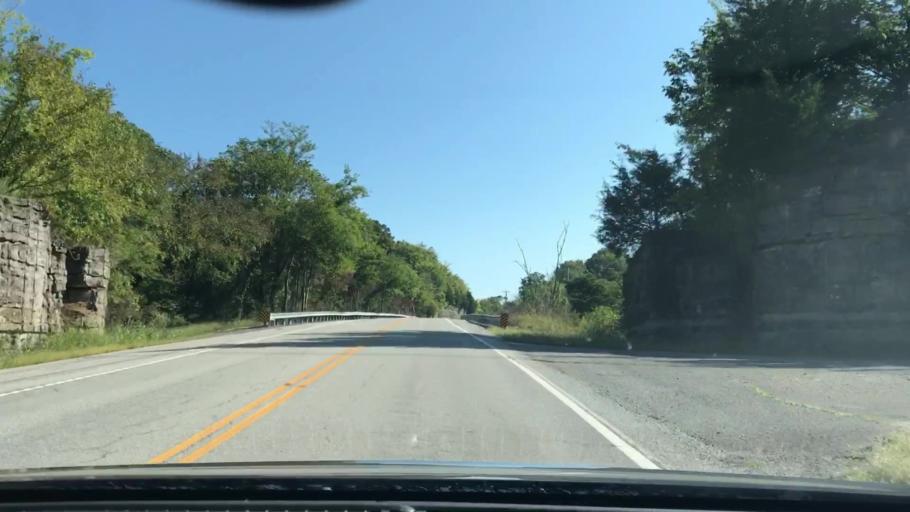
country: US
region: Tennessee
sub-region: Jackson County
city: Gainesboro
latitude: 36.3502
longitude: -85.7959
